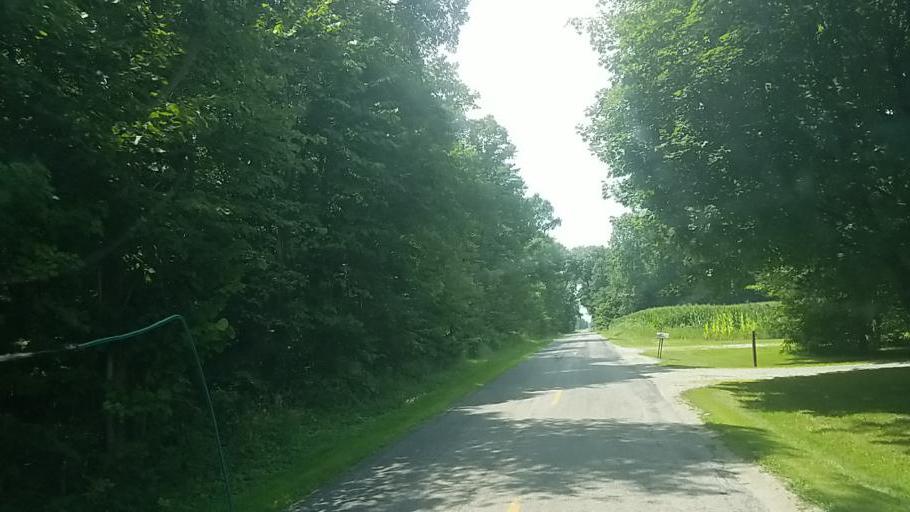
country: US
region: Ohio
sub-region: Union County
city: Richwood
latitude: 40.6074
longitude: -83.3311
